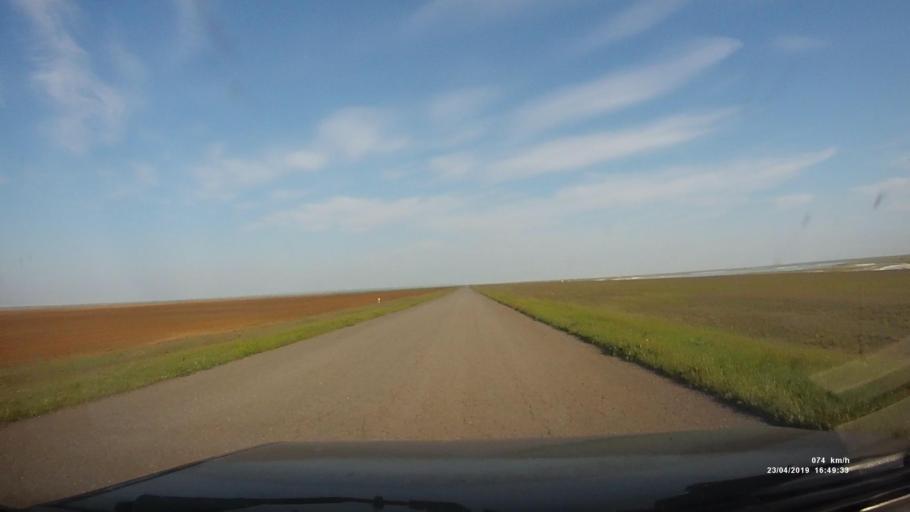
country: RU
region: Kalmykiya
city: Priyutnoye
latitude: 46.3305
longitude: 43.2783
